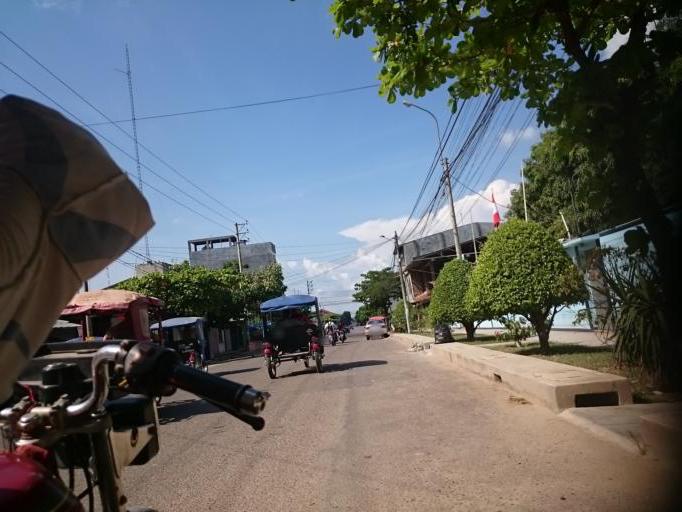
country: PE
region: Ucayali
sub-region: Provincia de Coronel Portillo
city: Pucallpa
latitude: -8.3808
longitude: -74.5325
